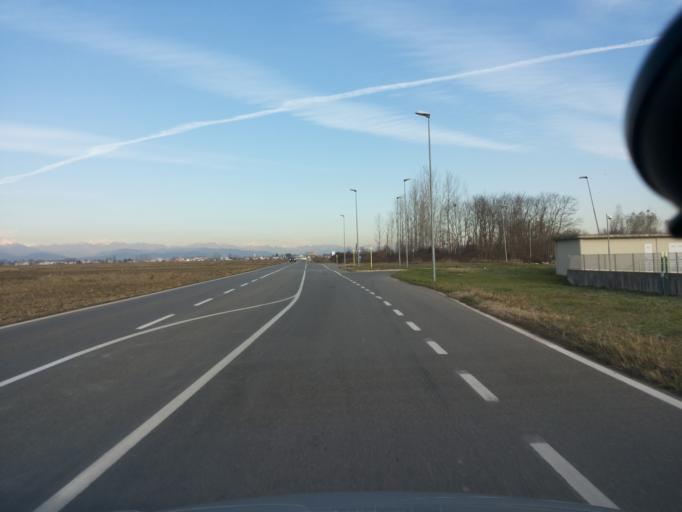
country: IT
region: Piedmont
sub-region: Provincia di Vercelli
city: Arborio
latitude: 45.4753
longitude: 8.3874
